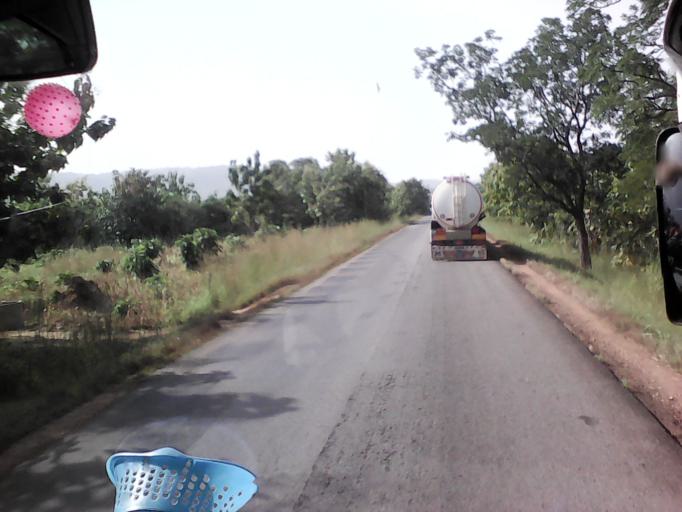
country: TG
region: Centrale
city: Sokode
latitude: 9.0839
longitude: 1.1357
